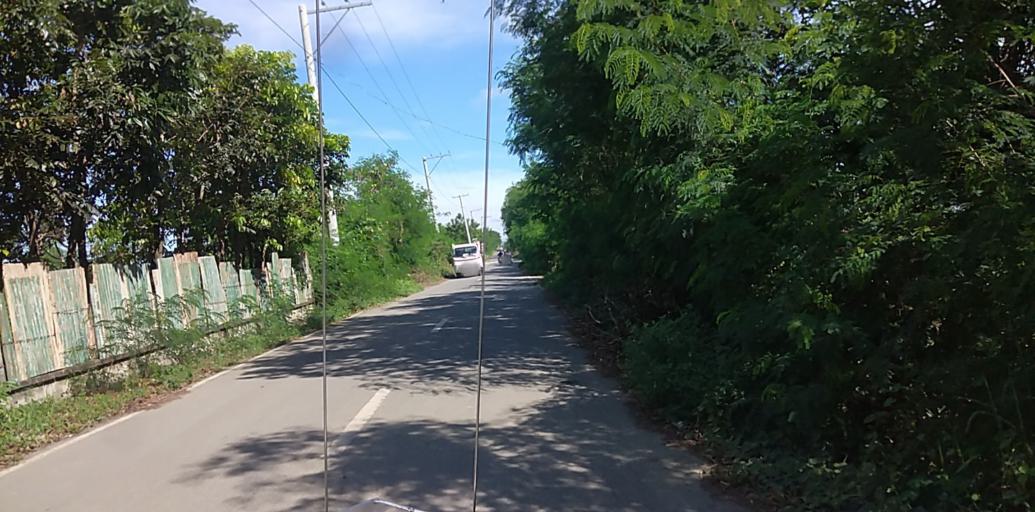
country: PH
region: Central Luzon
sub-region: Province of Pampanga
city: San Nicolas
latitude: 15.0712
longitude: 120.8062
